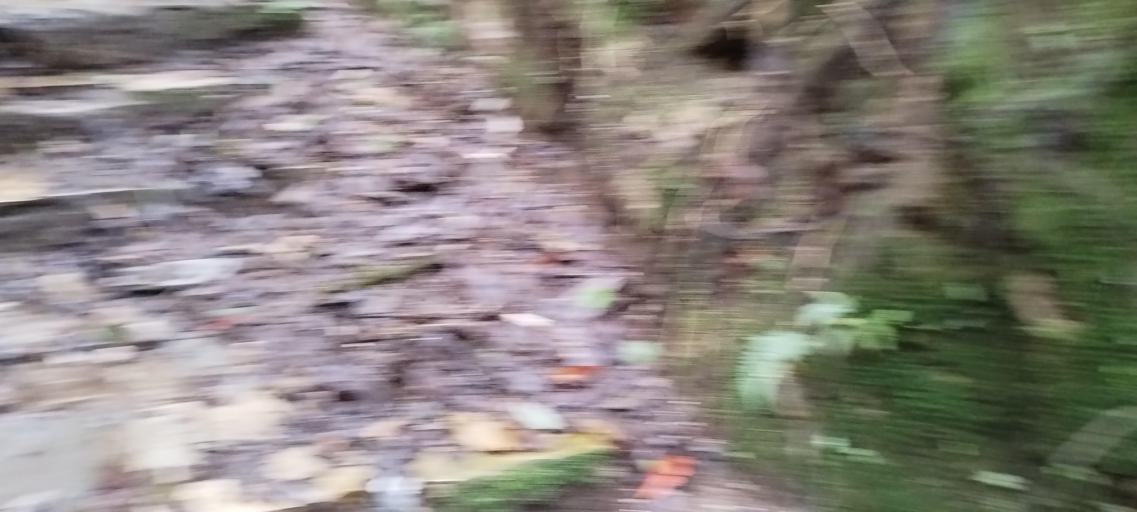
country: NP
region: Central Region
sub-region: Bagmati Zone
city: Kathmandu
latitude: 27.7892
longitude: 85.3836
